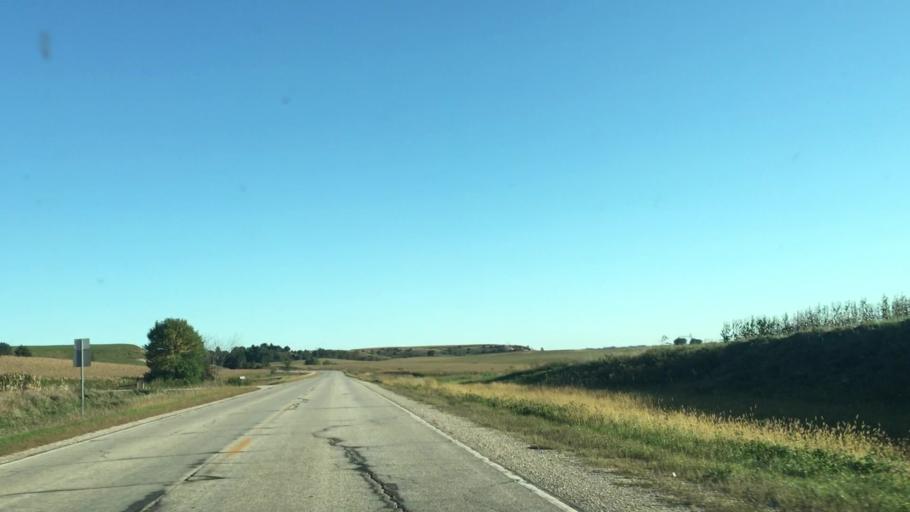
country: US
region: Minnesota
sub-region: Fillmore County
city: Chatfield
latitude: 43.8514
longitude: -92.1079
